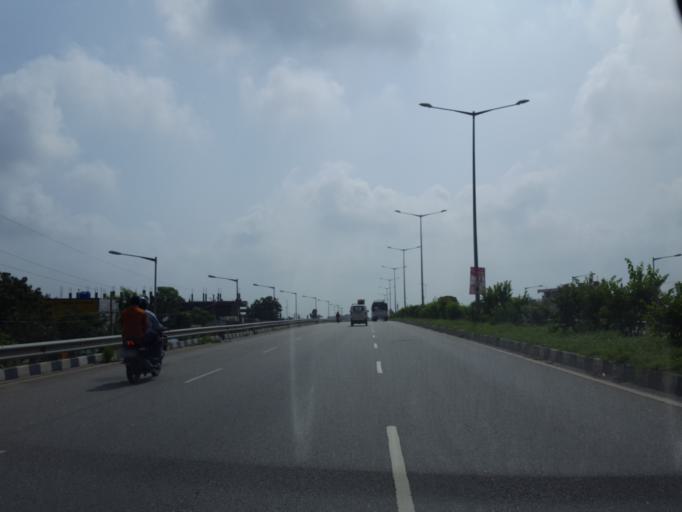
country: IN
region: Telangana
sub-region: Nalgonda
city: Gudur
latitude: 17.2616
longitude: 78.8422
